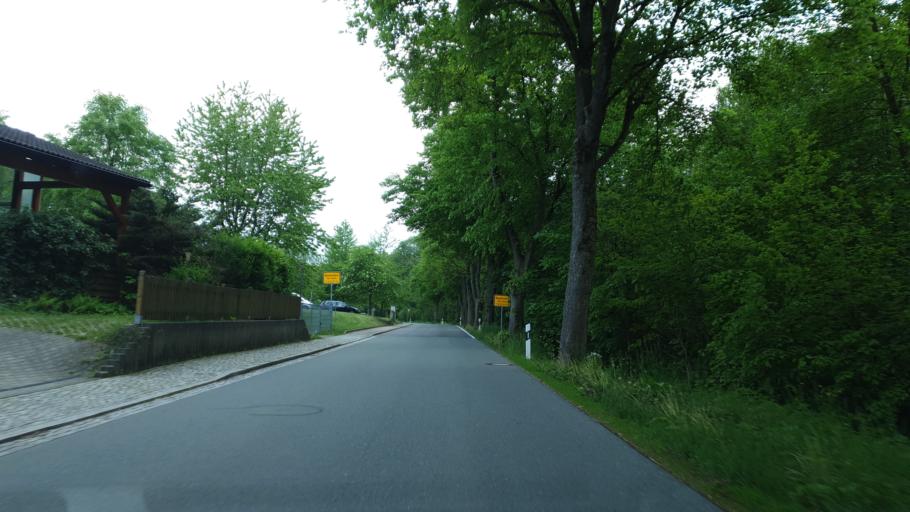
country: DE
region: Saxony
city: Lugau
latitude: 50.7185
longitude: 12.7448
